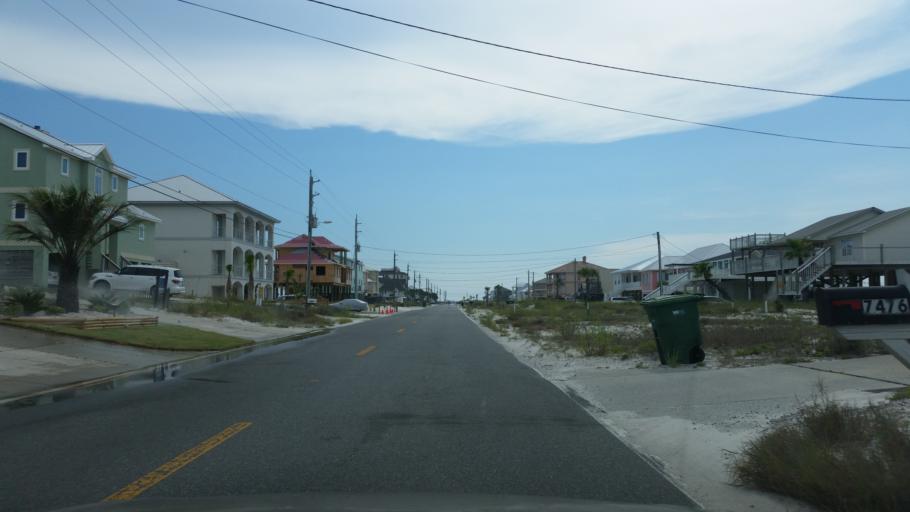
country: US
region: Florida
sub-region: Santa Rosa County
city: Navarre
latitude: 30.3730
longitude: -86.9109
